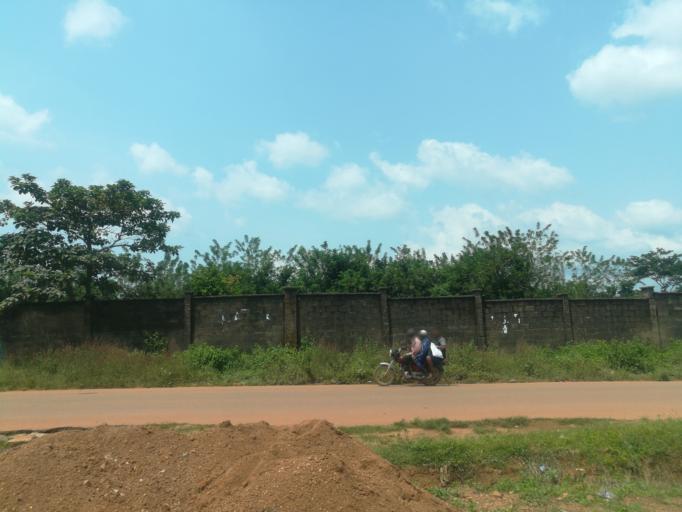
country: NG
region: Oyo
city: Moniya
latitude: 7.4708
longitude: 3.9569
